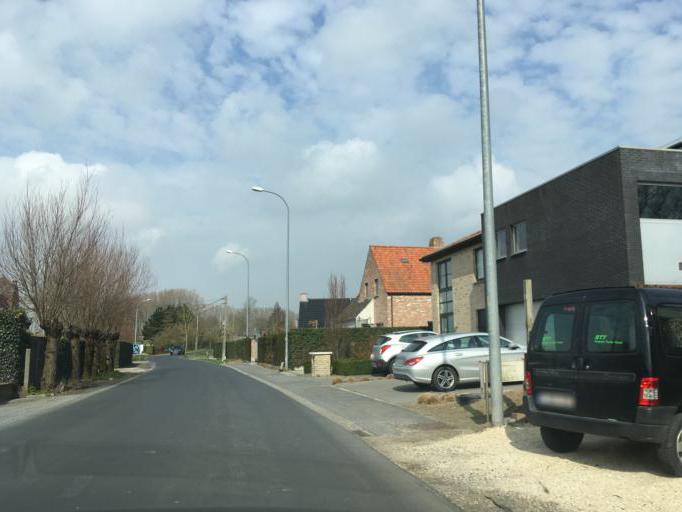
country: BE
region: Flanders
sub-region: Provincie West-Vlaanderen
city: Ardooie
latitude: 50.9427
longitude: 3.1792
